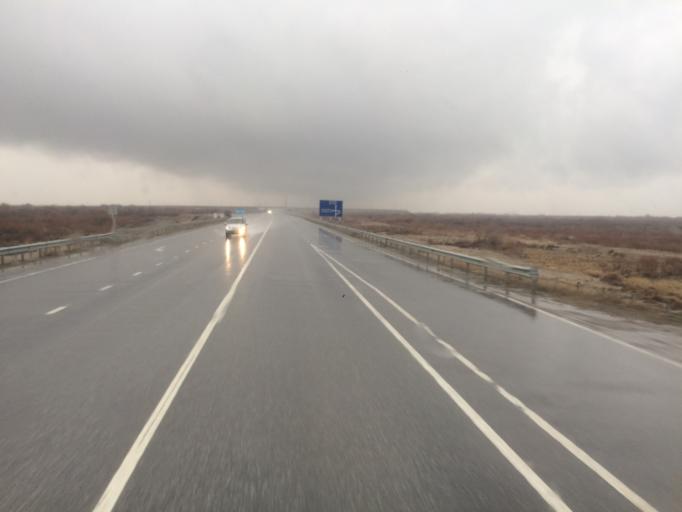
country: KZ
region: Qyzylorda
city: Terenozek
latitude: 44.8823
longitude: 65.1388
